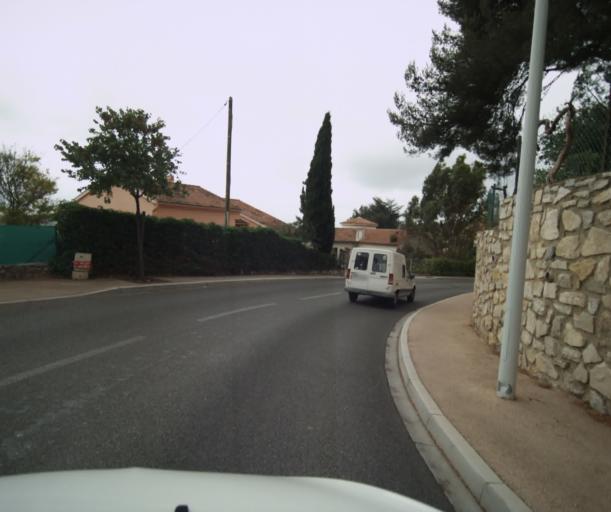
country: FR
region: Provence-Alpes-Cote d'Azur
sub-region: Departement du Var
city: La Garde
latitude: 43.1258
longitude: 5.9998
